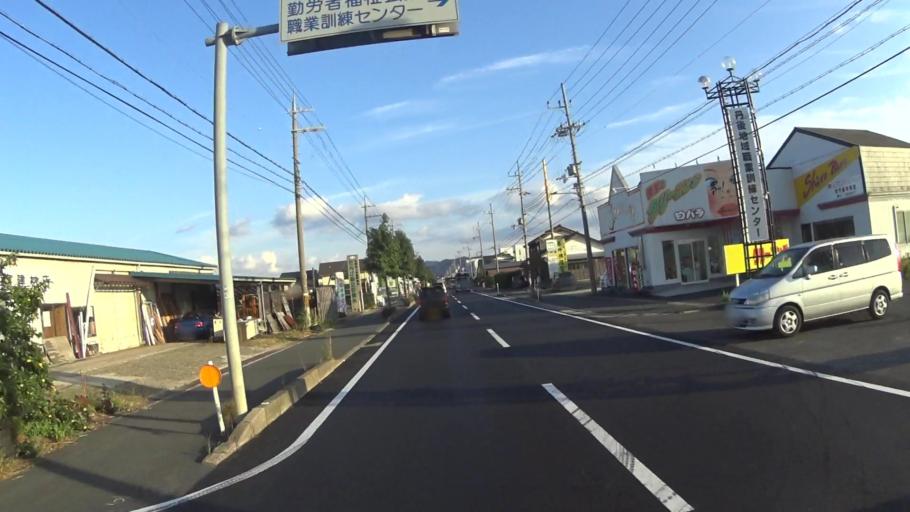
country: JP
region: Kyoto
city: Miyazu
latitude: 35.6036
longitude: 135.0843
